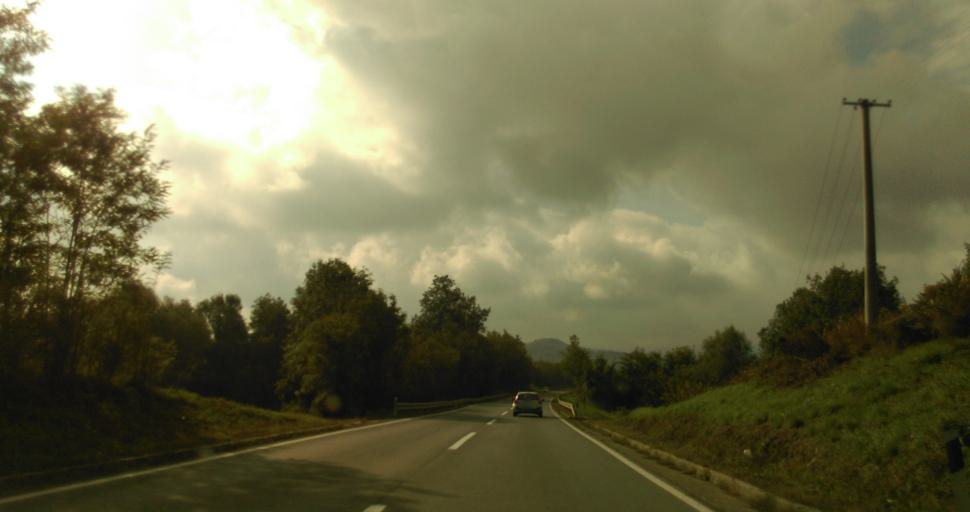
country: RS
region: Central Serbia
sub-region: Kolubarski Okrug
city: Ljig
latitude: 44.2585
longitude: 20.2864
